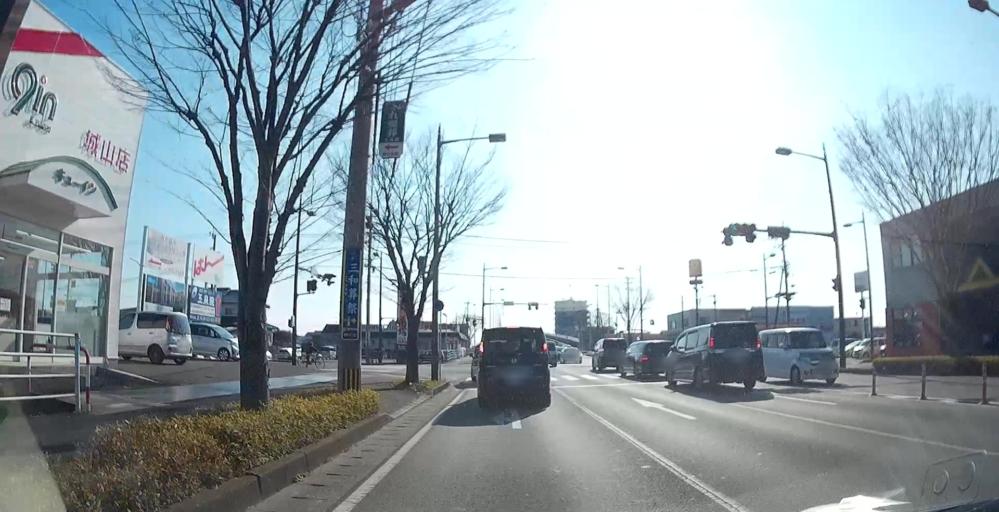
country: JP
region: Kumamoto
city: Kumamoto
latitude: 32.7765
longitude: 130.6730
